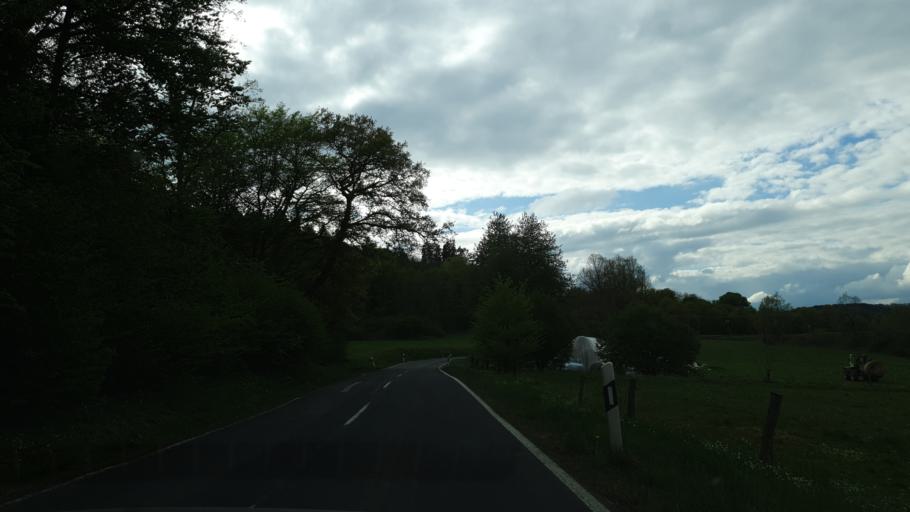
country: DE
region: Rheinland-Pfalz
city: Hardt
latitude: 50.6215
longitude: 7.9046
